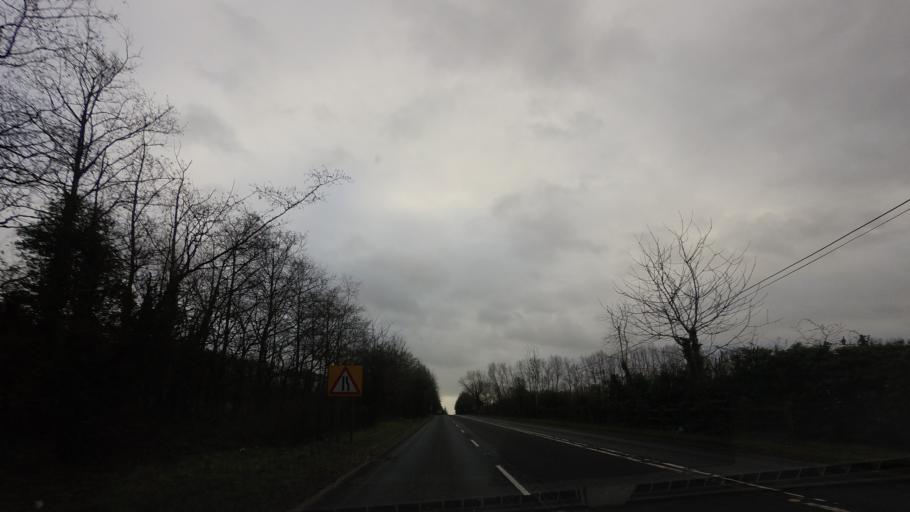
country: GB
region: England
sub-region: Kent
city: East Peckham
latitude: 51.2476
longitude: 0.3747
